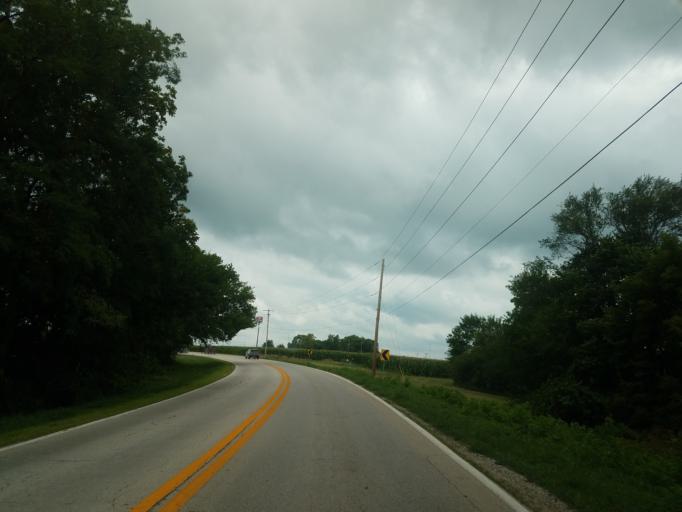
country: US
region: Illinois
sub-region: McLean County
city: Bloomington
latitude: 40.4838
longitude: -89.0315
